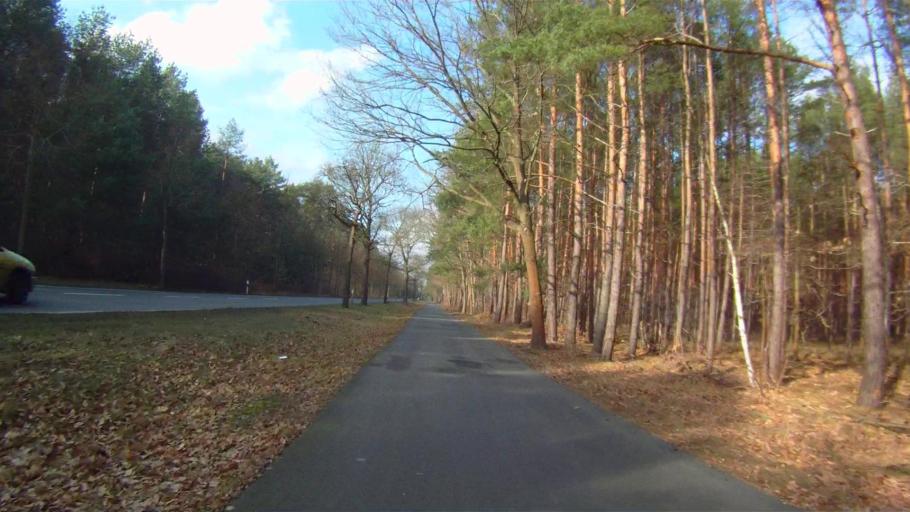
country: DE
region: Brandenburg
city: Zeuthen
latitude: 52.3923
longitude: 13.6198
